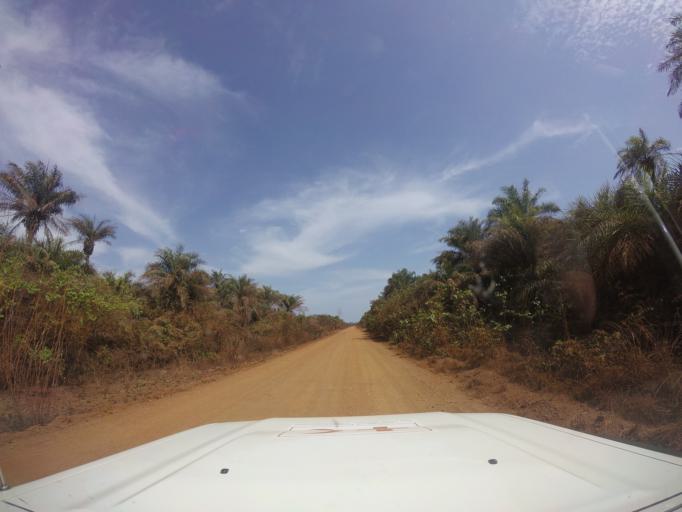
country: LR
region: Grand Cape Mount
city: Robertsport
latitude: 6.6983
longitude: -11.2866
